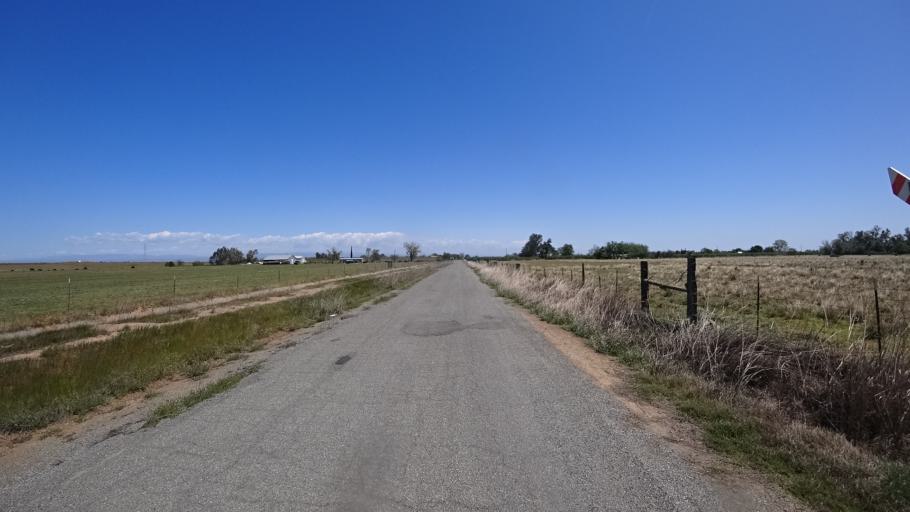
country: US
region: California
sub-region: Glenn County
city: Orland
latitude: 39.7949
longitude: -122.2190
